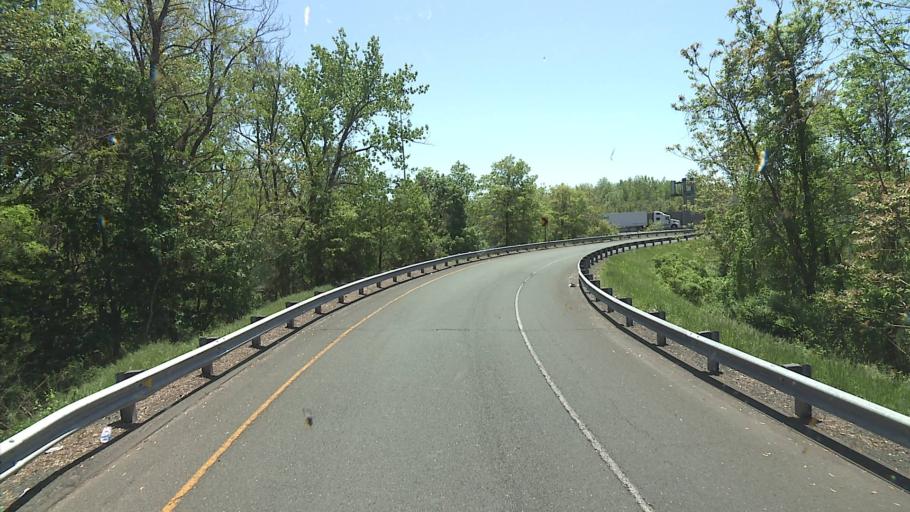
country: US
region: Connecticut
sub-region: Hartford County
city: East Hartford
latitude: 41.7650
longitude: -72.6437
